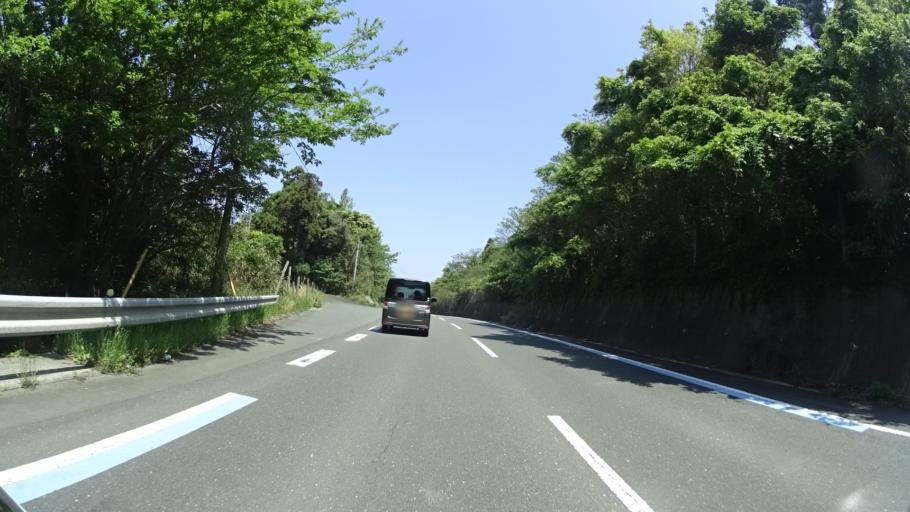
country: JP
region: Ehime
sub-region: Nishiuwa-gun
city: Ikata-cho
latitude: 33.5331
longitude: 132.3991
